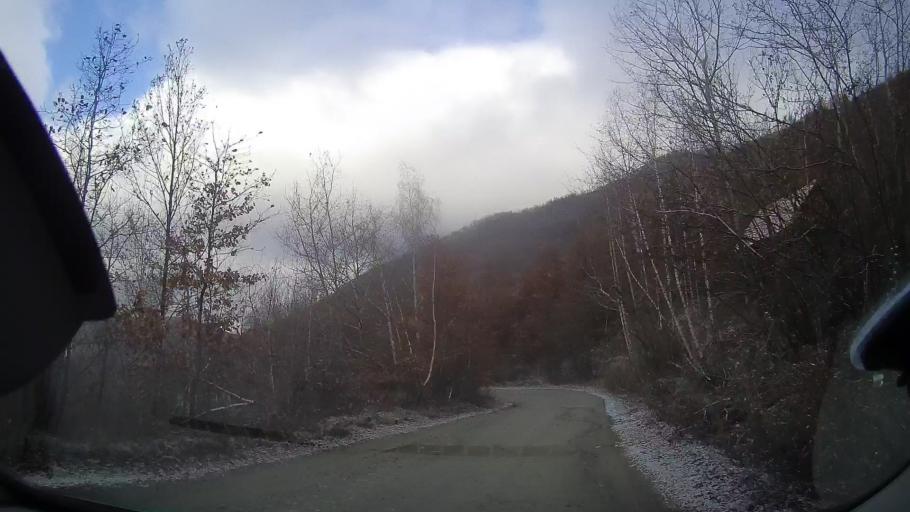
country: RO
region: Cluj
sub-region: Comuna Valea Ierii
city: Valea Ierii
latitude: 46.6728
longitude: 23.3174
